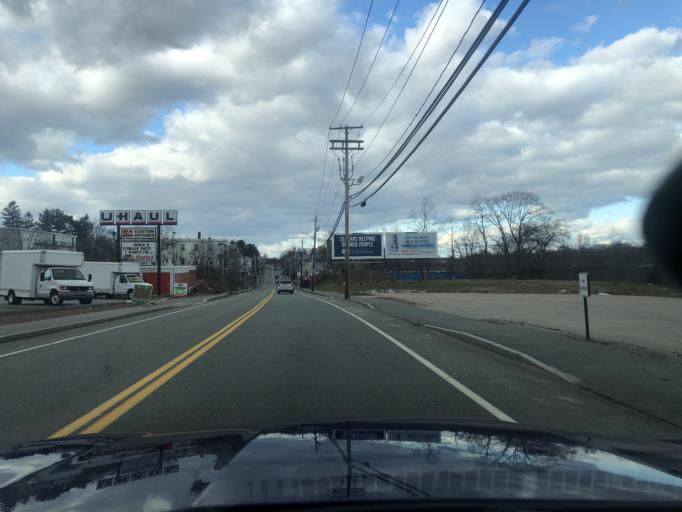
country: US
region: Massachusetts
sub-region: Plymouth County
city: Brockton
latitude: 42.1004
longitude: -71.0184
